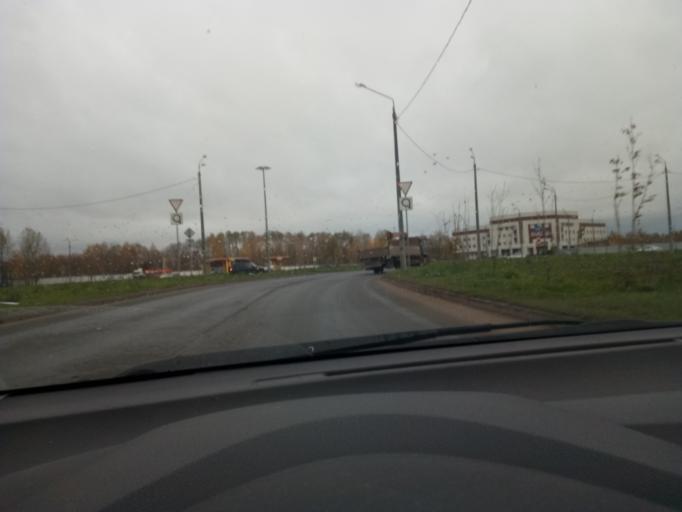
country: RU
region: Tatarstan
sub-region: Gorod Kazan'
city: Kazan
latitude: 55.8511
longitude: 49.1312
